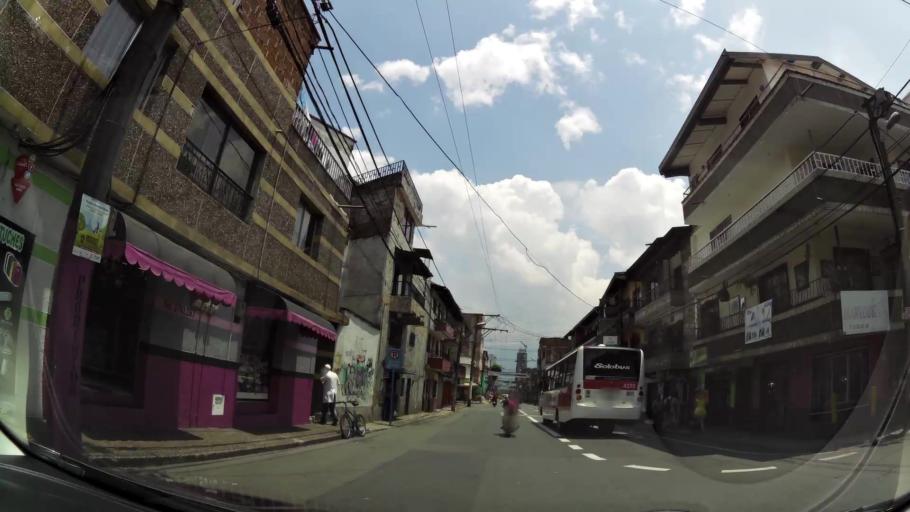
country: CO
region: Antioquia
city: Sabaneta
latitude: 6.1687
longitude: -75.6143
